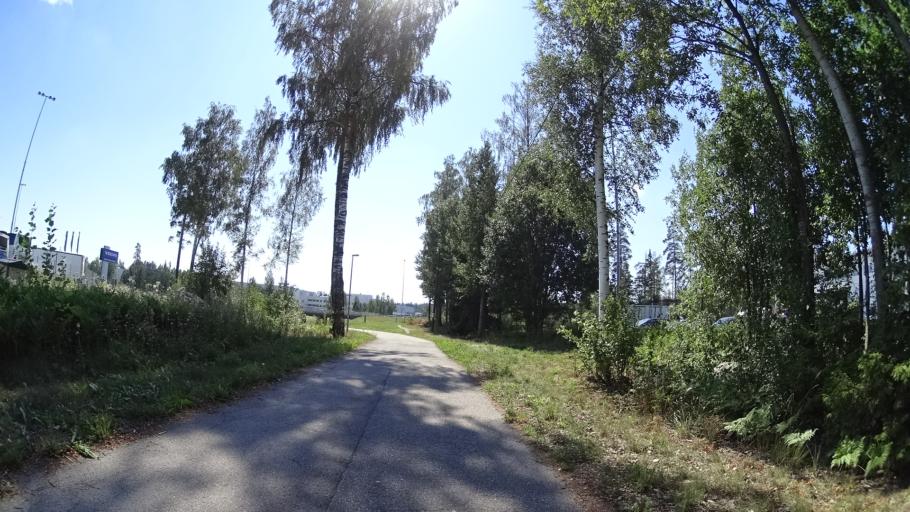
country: FI
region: Uusimaa
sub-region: Helsinki
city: Vantaa
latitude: 60.2982
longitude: 24.9317
